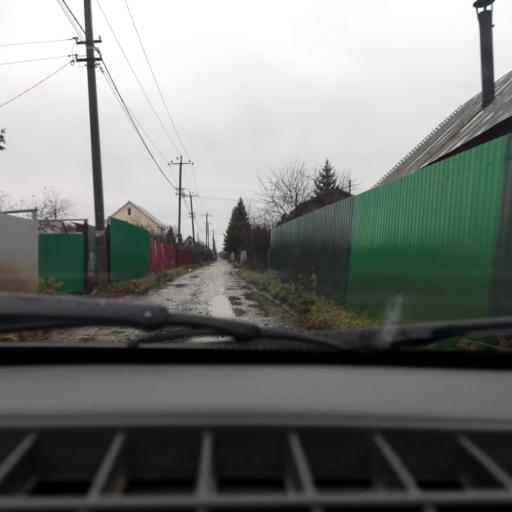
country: RU
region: Bashkortostan
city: Avdon
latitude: 54.6252
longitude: 55.7196
